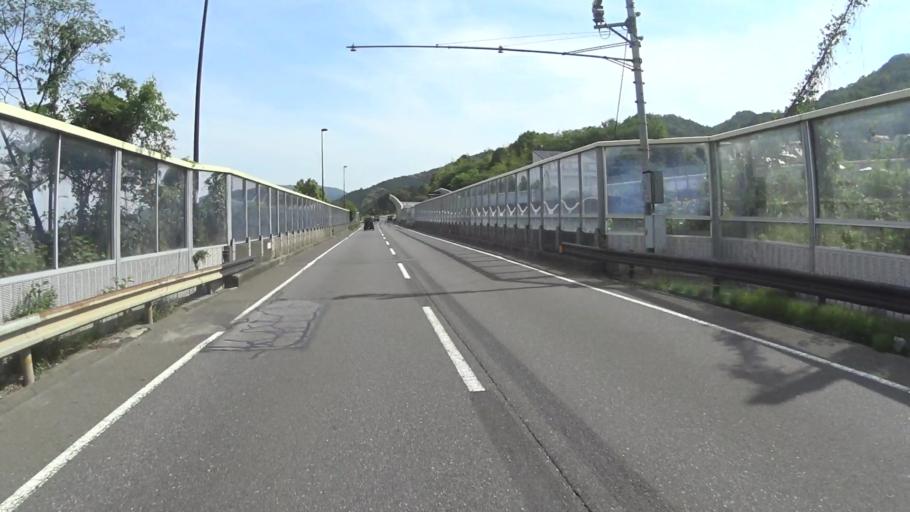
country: JP
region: Shiga Prefecture
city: Otsu-shi
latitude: 35.0304
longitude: 135.8501
